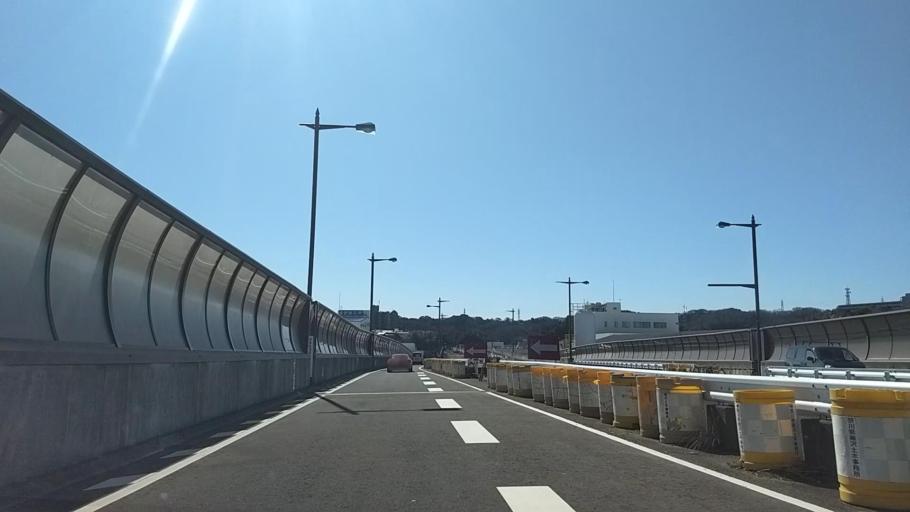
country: JP
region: Kanagawa
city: Fujisawa
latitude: 35.3359
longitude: 139.5016
